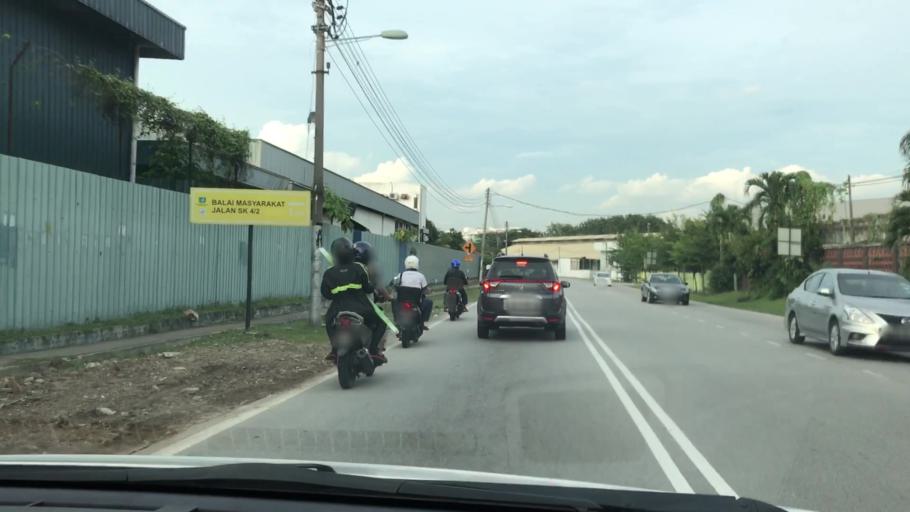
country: MY
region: Selangor
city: Kampong Baharu Balakong
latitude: 3.0142
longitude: 101.7018
